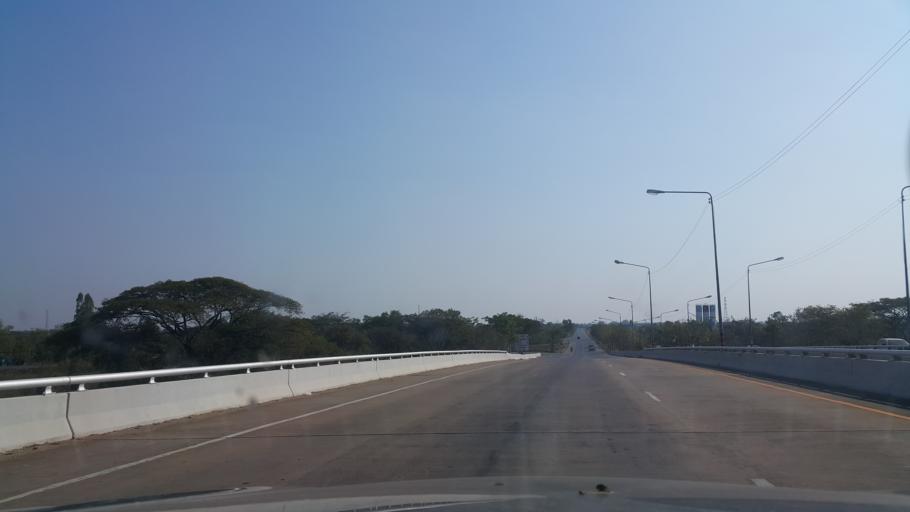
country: TH
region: Khon Kaen
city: Khon Kaen
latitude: 16.4371
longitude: 102.9179
